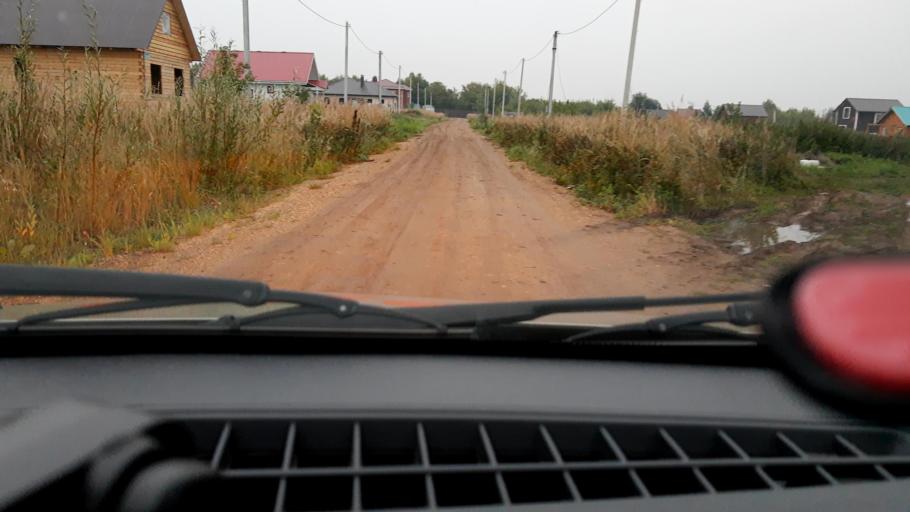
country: RU
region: Bashkortostan
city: Kabakovo
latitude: 54.5777
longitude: 56.2820
